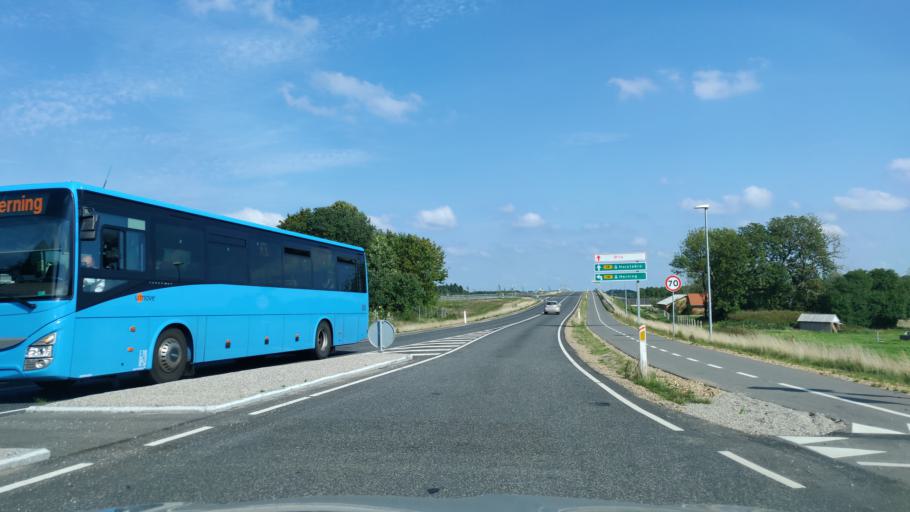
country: DK
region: Central Jutland
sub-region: Herning Kommune
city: Avlum
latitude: 56.2167
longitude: 8.8472
